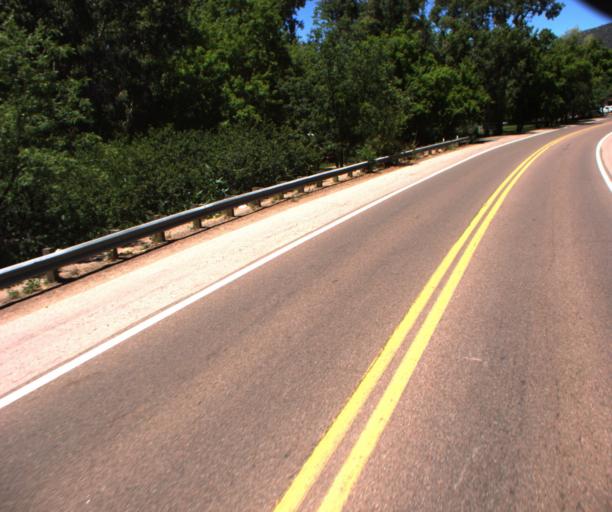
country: US
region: Arizona
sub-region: Gila County
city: Pine
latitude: 34.3836
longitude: -111.4539
